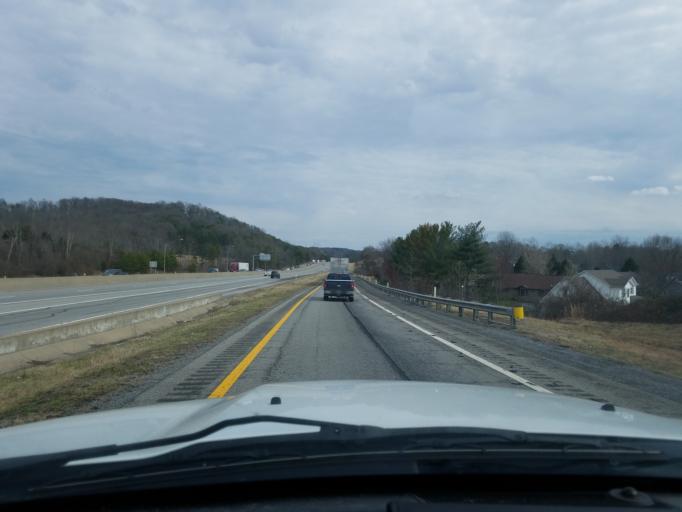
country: US
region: West Virginia
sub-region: Putnam County
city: Teays Valley
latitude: 38.4542
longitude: -81.8979
